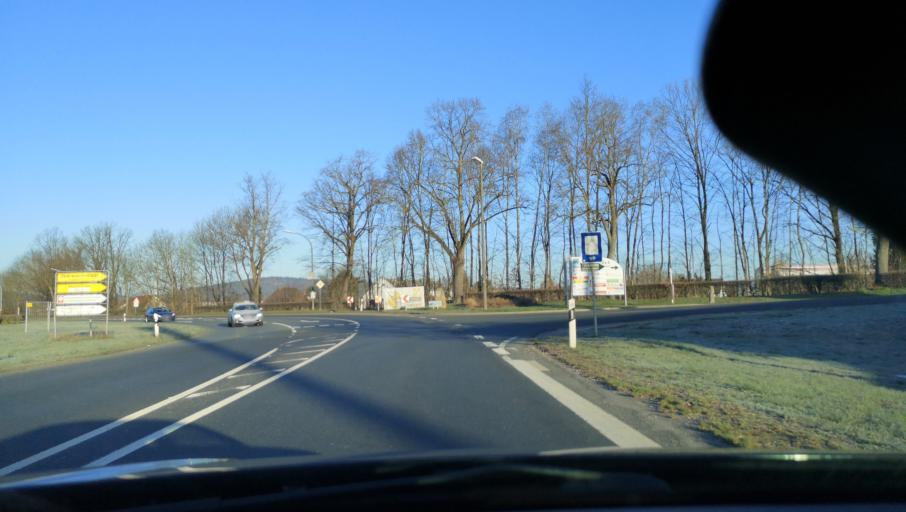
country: DE
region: Bavaria
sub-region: Upper Franconia
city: Lichtenfels
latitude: 50.1499
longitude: 11.0816
